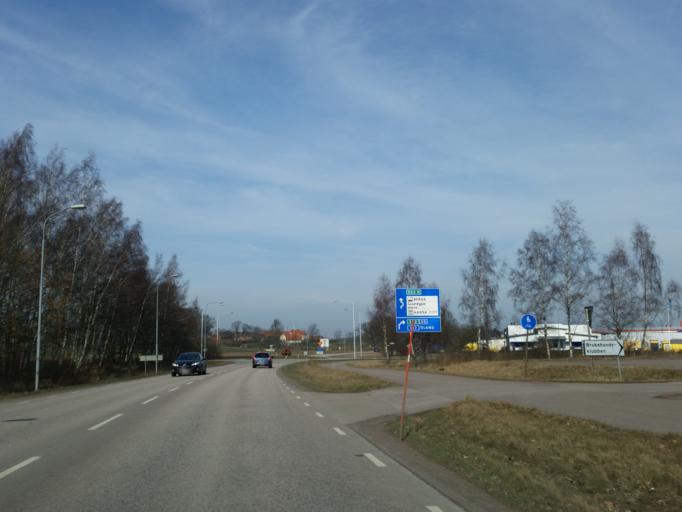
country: SE
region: Kalmar
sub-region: Kalmar Kommun
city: Kalmar
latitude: 56.6798
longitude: 16.3158
